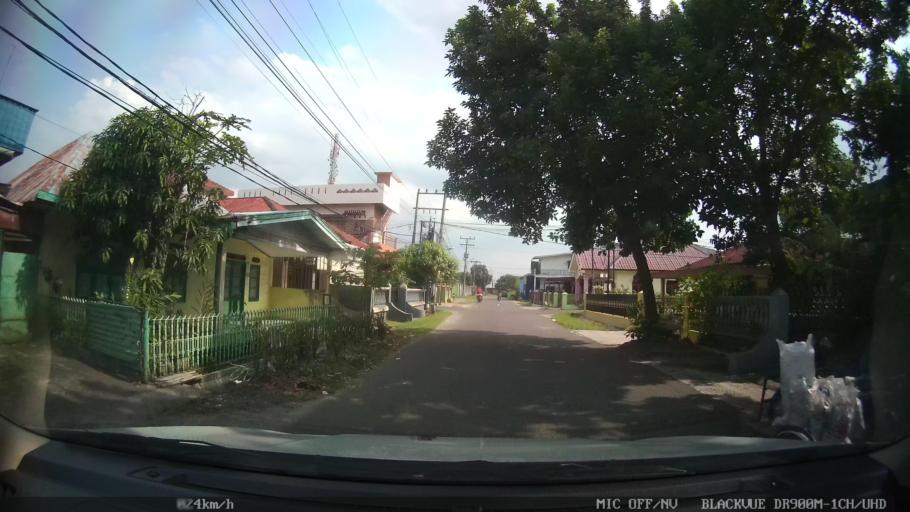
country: ID
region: North Sumatra
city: Binjai
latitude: 3.6073
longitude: 98.5018
